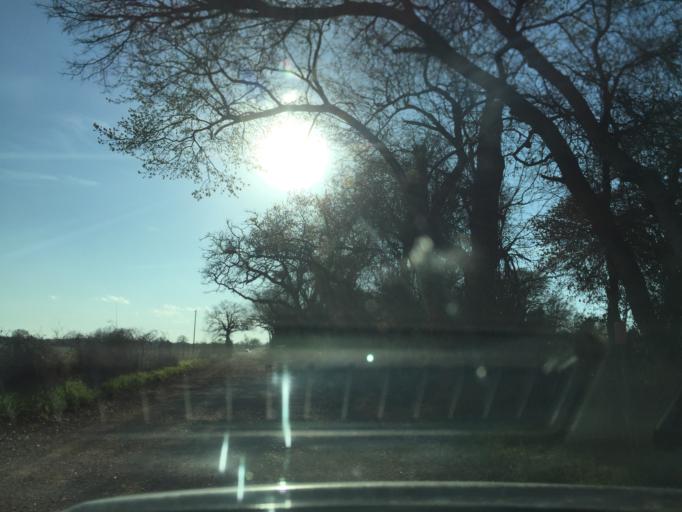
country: US
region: Texas
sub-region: Bastrop County
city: Elgin
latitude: 30.4123
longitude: -97.2267
